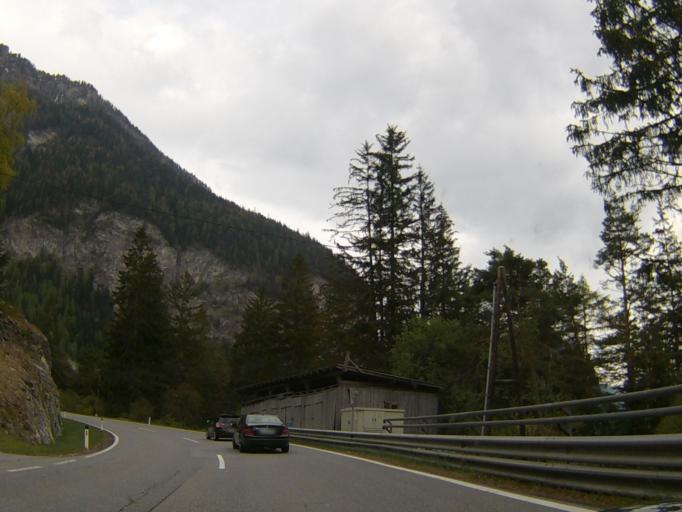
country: AT
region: Tyrol
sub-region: Politischer Bezirk Landeck
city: Nauders
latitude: 46.9322
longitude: 10.4885
